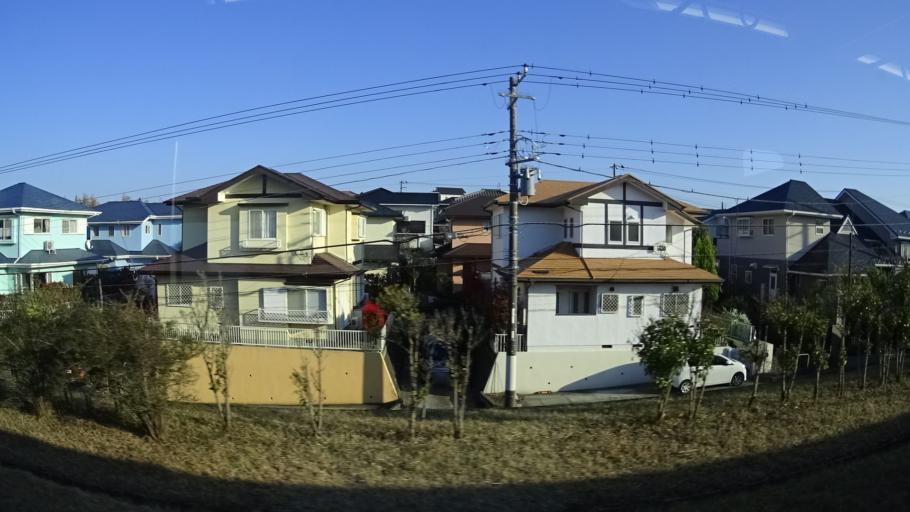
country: JP
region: Kanagawa
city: Miura
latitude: 35.1811
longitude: 139.6372
